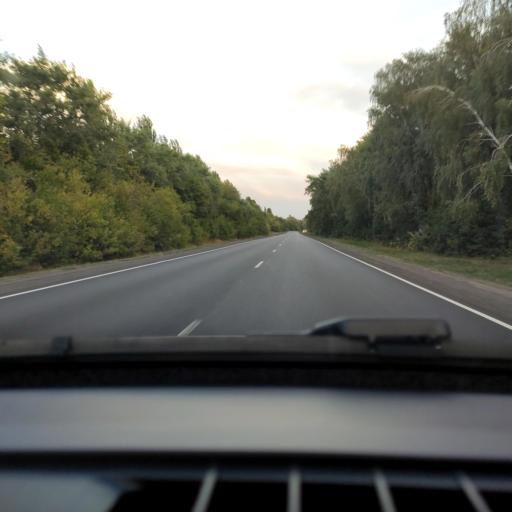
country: RU
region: Voronezj
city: Panino
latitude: 51.4810
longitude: 39.9652
